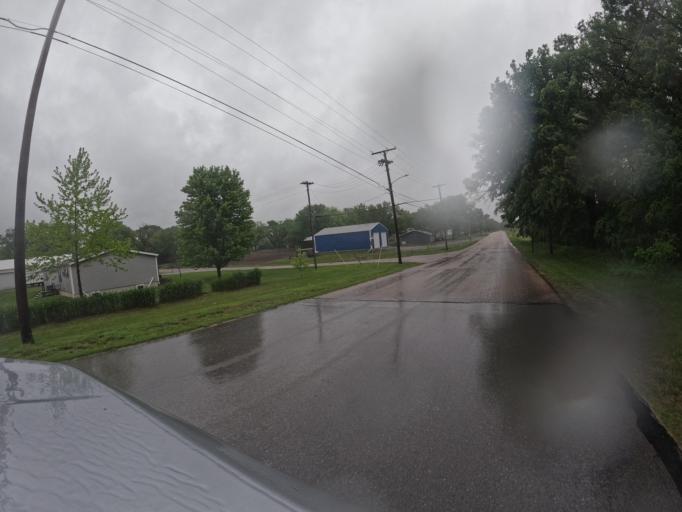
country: US
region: Nebraska
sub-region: Gage County
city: Wymore
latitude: 40.1224
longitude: -96.6578
